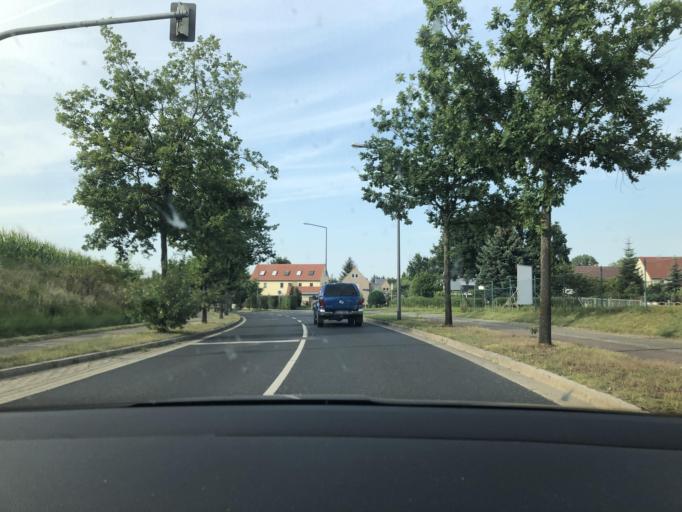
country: DE
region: Saxony
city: Albertstadt
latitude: 51.1190
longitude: 13.7316
